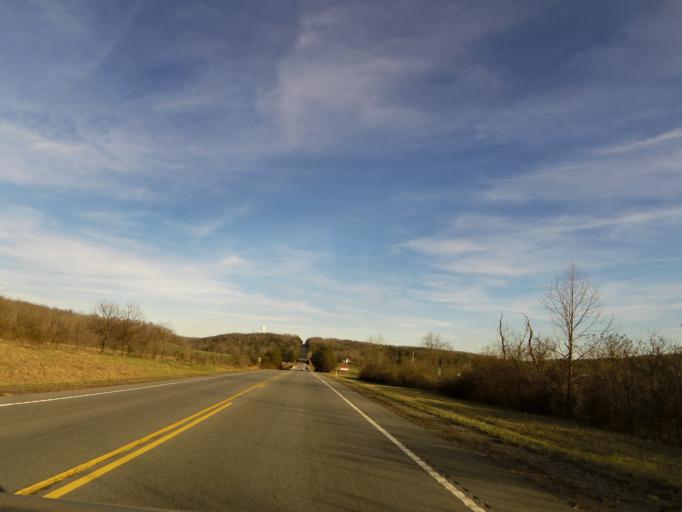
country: US
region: Tennessee
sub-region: Cumberland County
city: Crossville
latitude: 35.9680
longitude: -85.1492
